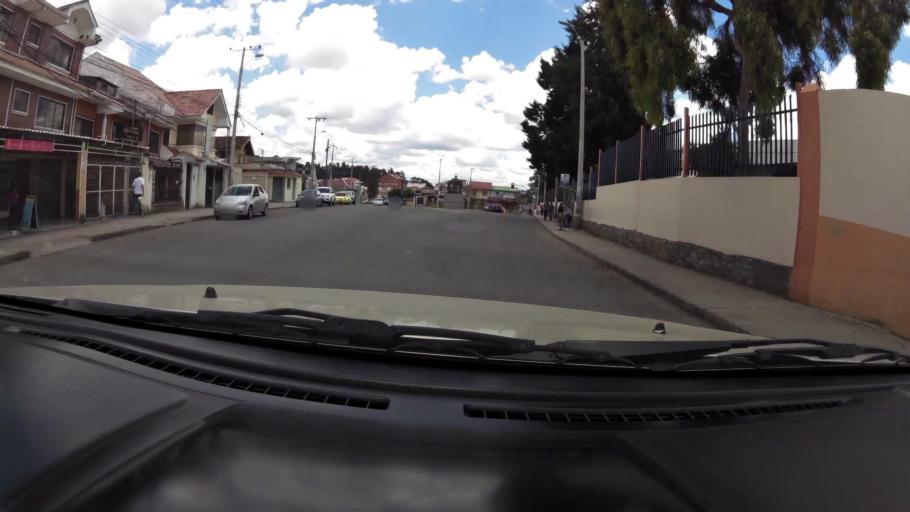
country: EC
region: Azuay
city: Cuenca
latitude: -2.9162
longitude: -79.0168
